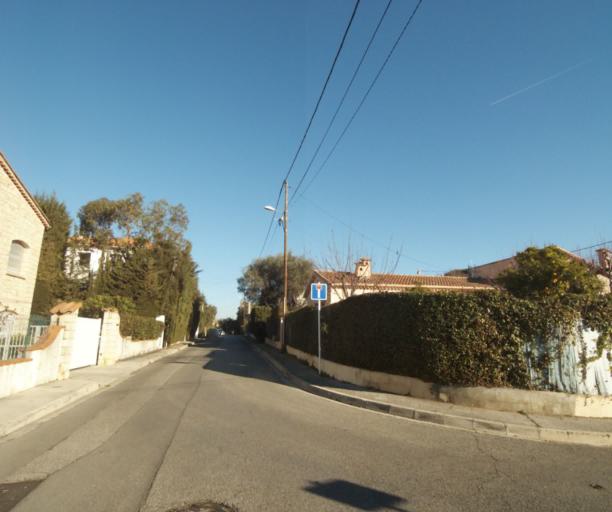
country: FR
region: Provence-Alpes-Cote d'Azur
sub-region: Departement des Alpes-Maritimes
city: Antibes
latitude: 43.5809
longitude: 7.1025
